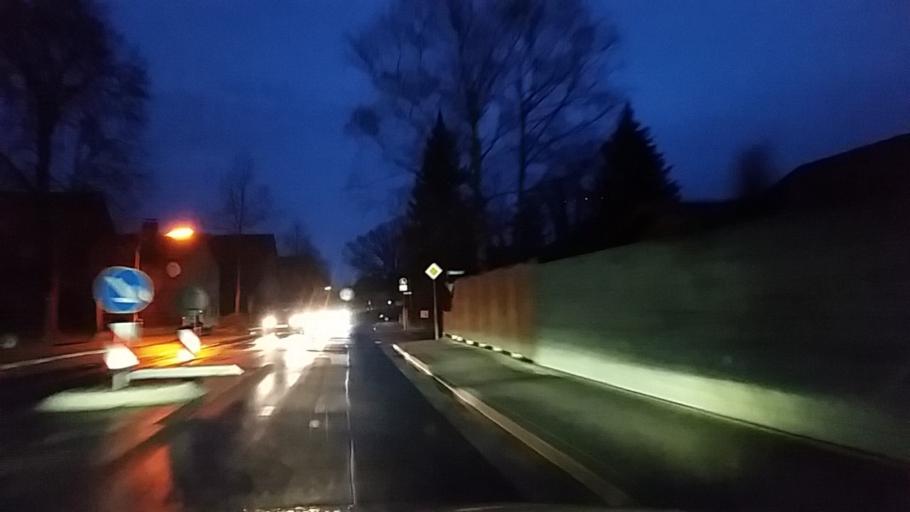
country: DE
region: Lower Saxony
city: Meine
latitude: 52.3536
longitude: 10.5579
